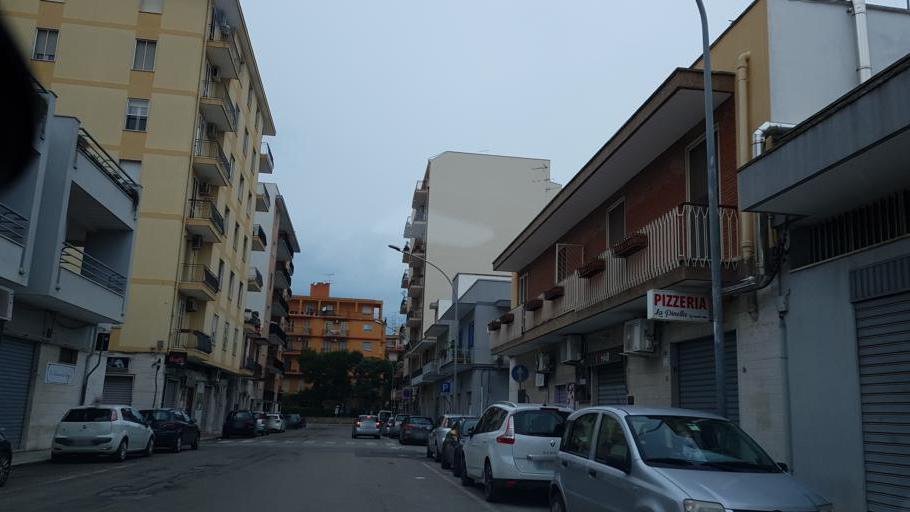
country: IT
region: Apulia
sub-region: Provincia di Brindisi
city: Brindisi
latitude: 40.6312
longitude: 17.9244
